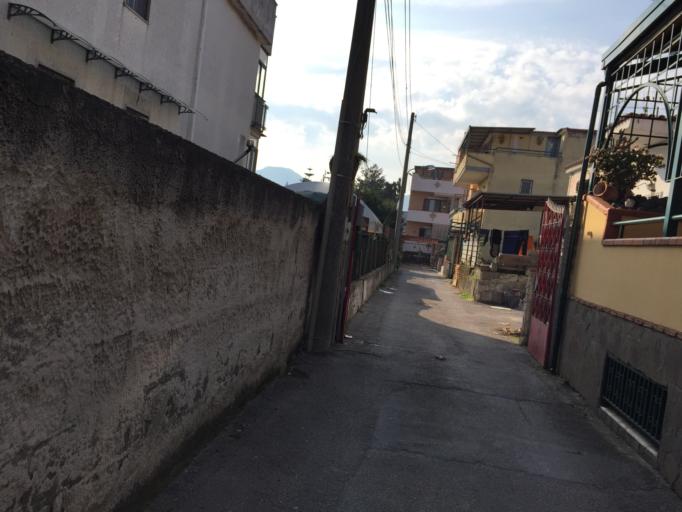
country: IT
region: Campania
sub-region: Provincia di Napoli
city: Pompei
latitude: 40.7546
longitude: 14.4973
